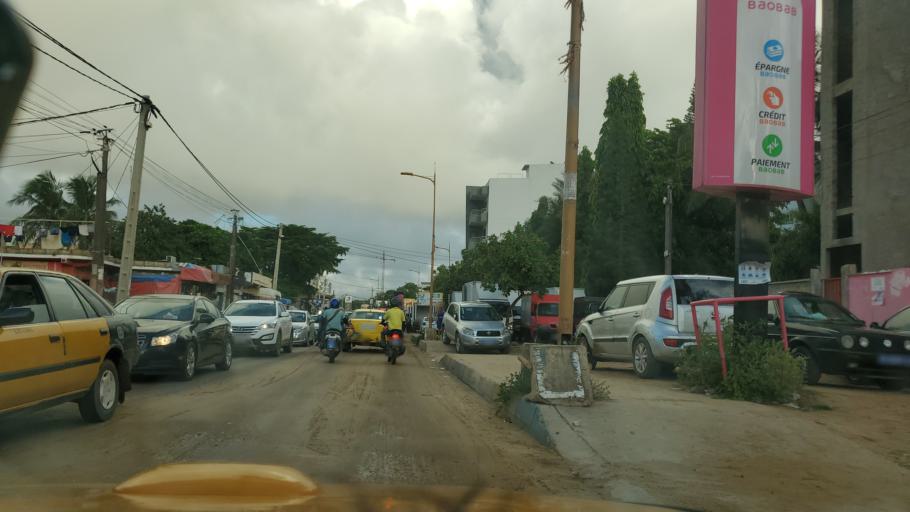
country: SN
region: Dakar
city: Mermoz Boabab
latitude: 14.7191
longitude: -17.4895
